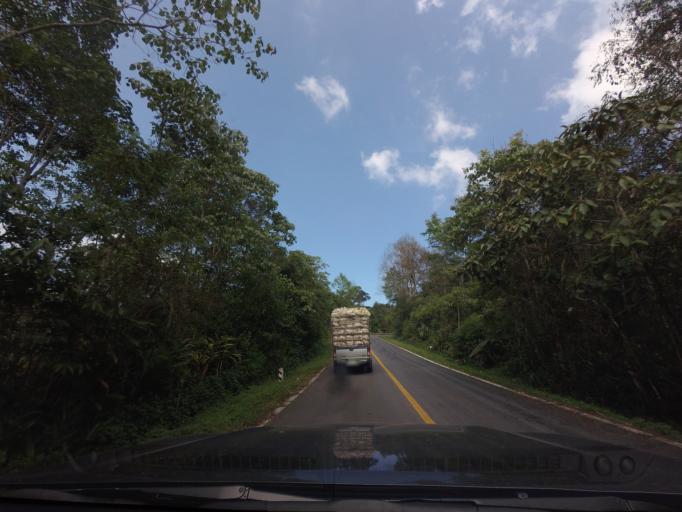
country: TH
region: Phetchabun
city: Lom Kao
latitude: 16.9657
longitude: 101.0192
